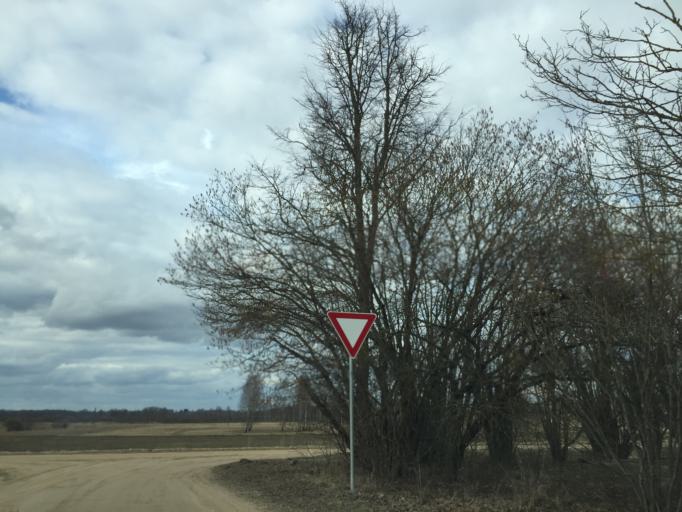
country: LV
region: Lielvarde
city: Lielvarde
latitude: 56.5126
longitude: 24.7372
